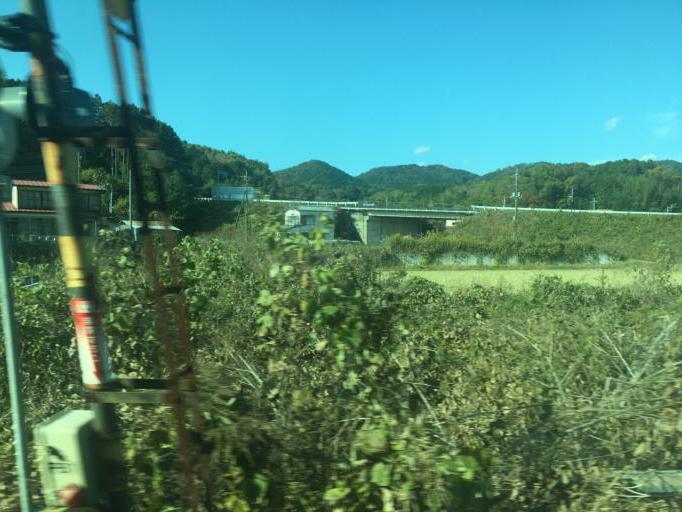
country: JP
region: Ibaraki
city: Kasama
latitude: 36.3526
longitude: 140.1899
